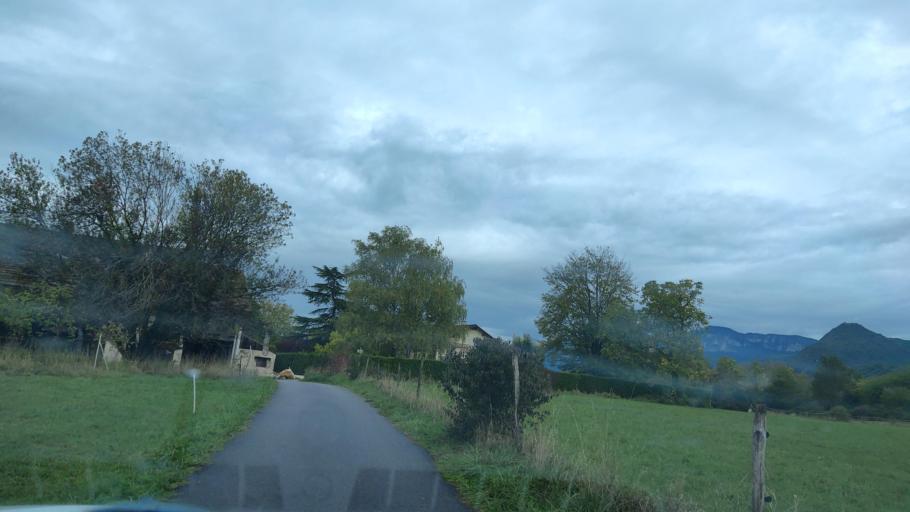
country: FR
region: Rhone-Alpes
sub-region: Departement de la Savoie
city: Les Marches
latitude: 45.5093
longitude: 5.9947
